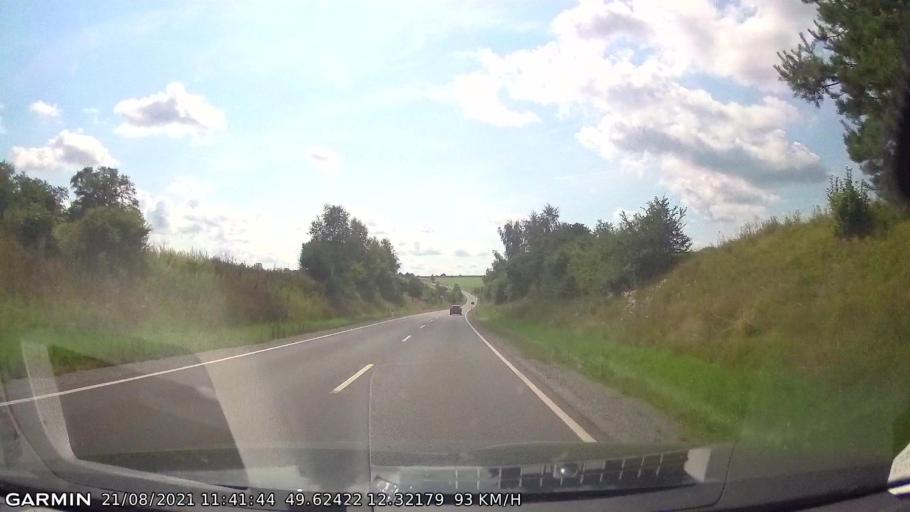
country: DE
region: Bavaria
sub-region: Upper Palatinate
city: Vohenstrauss
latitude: 49.6242
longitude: 12.3218
